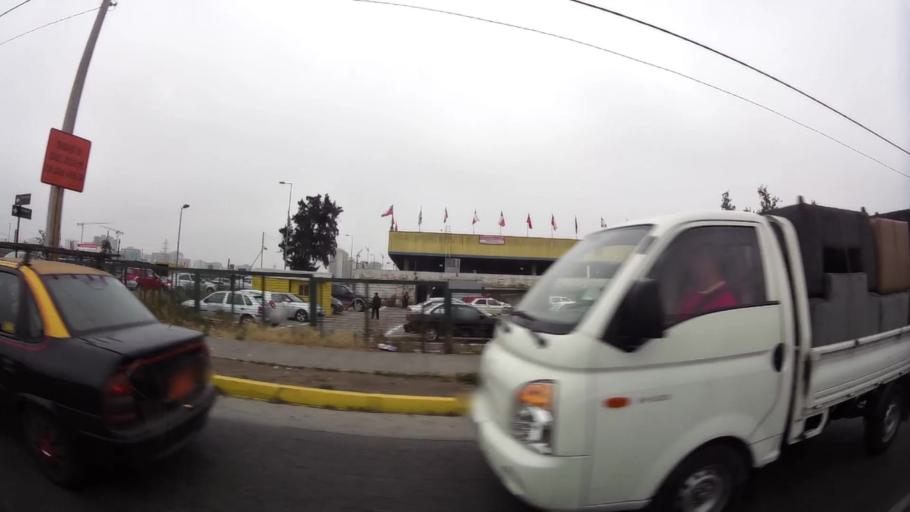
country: CL
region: Santiago Metropolitan
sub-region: Provincia de Santiago
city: Santiago
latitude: -33.4762
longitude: -70.6437
